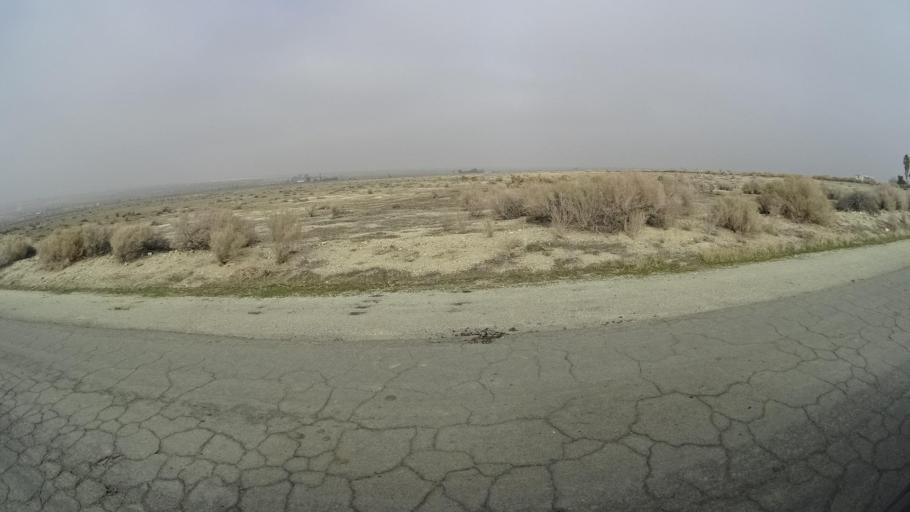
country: US
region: California
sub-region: Kern County
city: Maricopa
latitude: 35.0379
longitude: -119.3685
